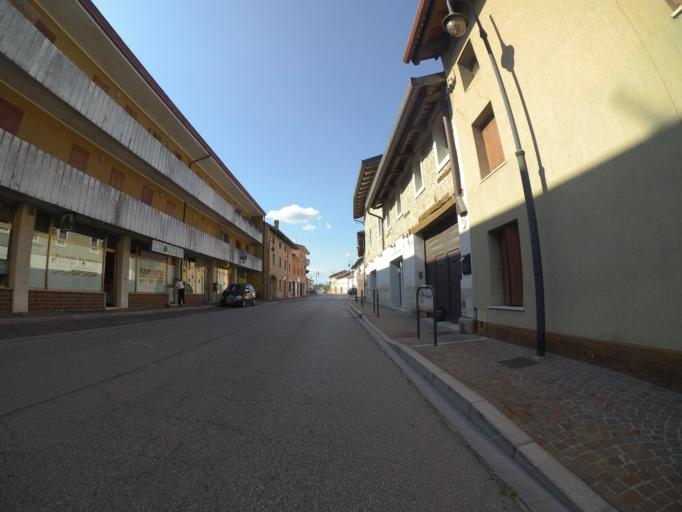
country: IT
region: Friuli Venezia Giulia
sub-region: Provincia di Udine
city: Mortegliano
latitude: 45.9467
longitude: 13.1718
